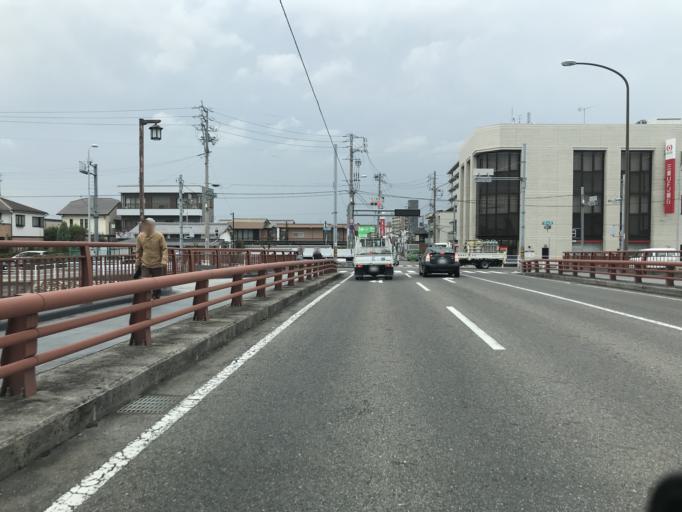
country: JP
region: Aichi
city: Nagoya-shi
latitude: 35.1949
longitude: 136.8507
